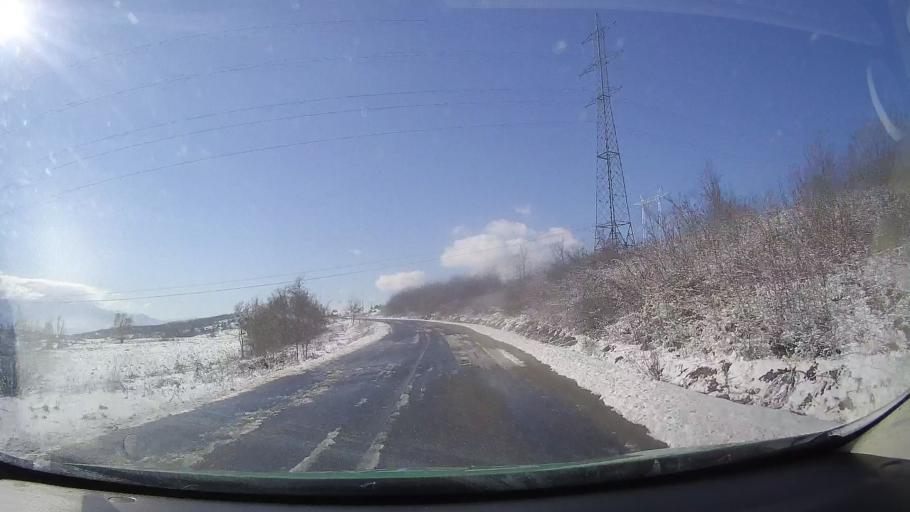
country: RO
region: Sibiu
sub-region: Comuna Avrig
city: Avrig
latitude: 45.7738
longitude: 24.3768
